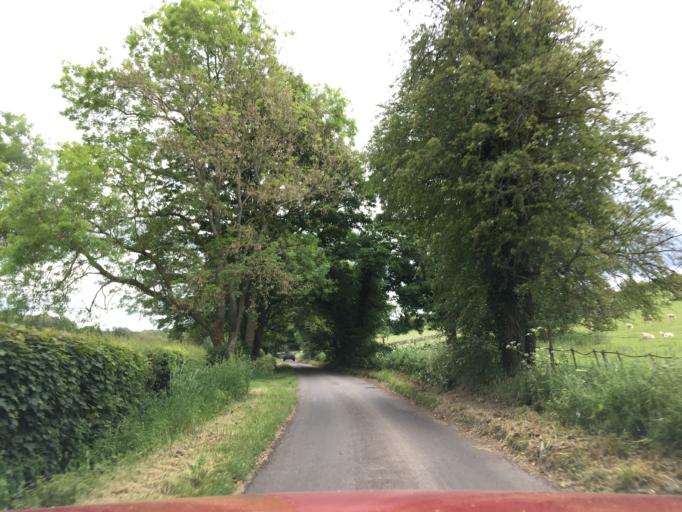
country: GB
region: England
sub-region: Gloucestershire
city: Cirencester
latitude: 51.7563
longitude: -1.9821
